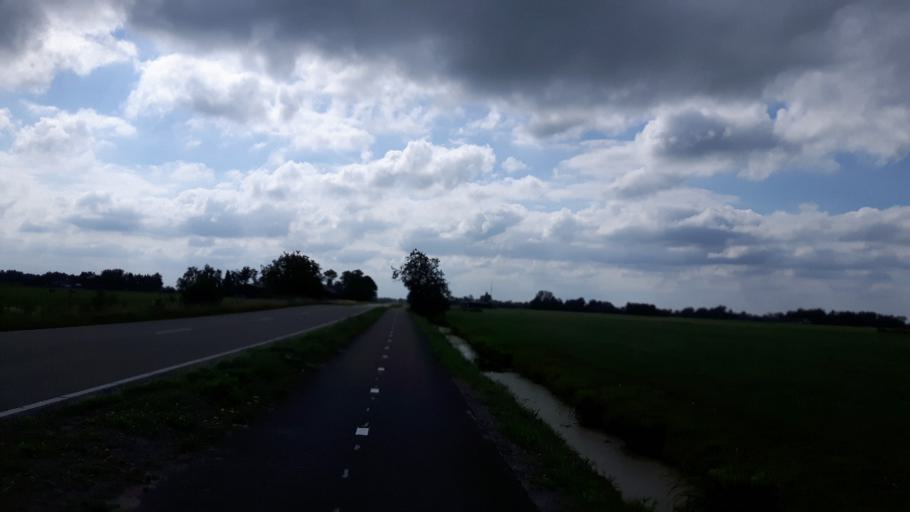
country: NL
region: Utrecht
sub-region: Gemeente Woerden
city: Woerden
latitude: 52.1321
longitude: 4.8589
